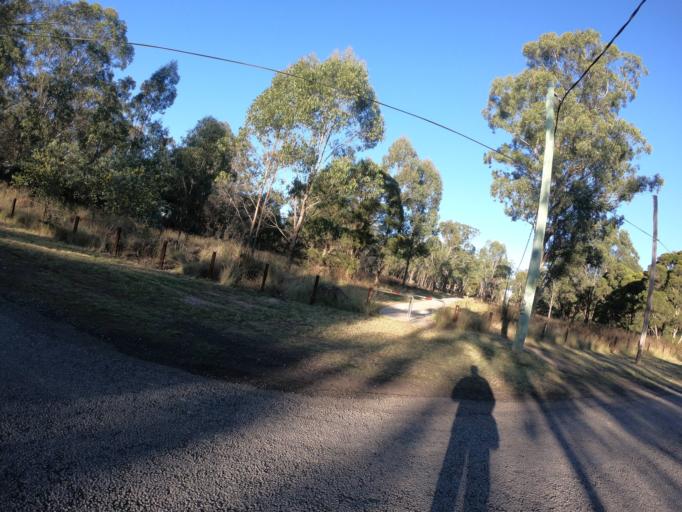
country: AU
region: New South Wales
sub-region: Hawkesbury
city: South Windsor
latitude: -33.6357
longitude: 150.8105
